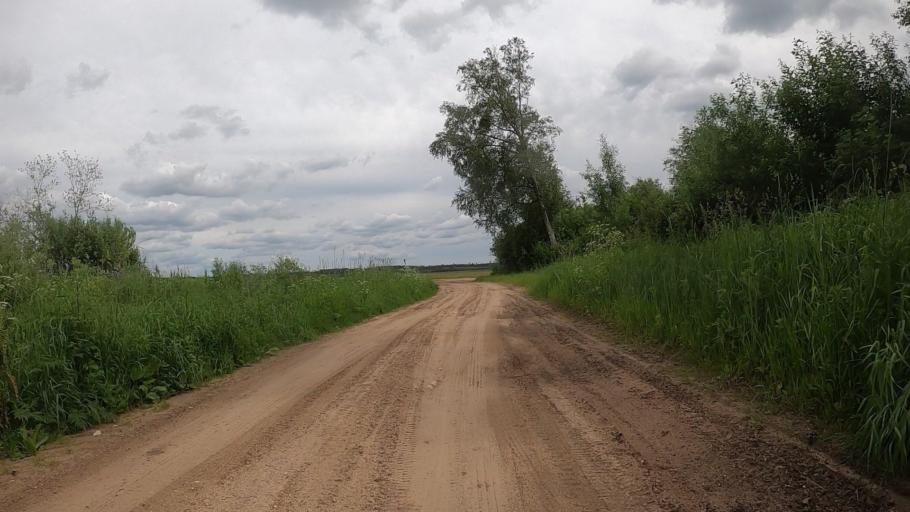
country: LV
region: Olaine
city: Olaine
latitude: 56.8267
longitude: 23.9406
